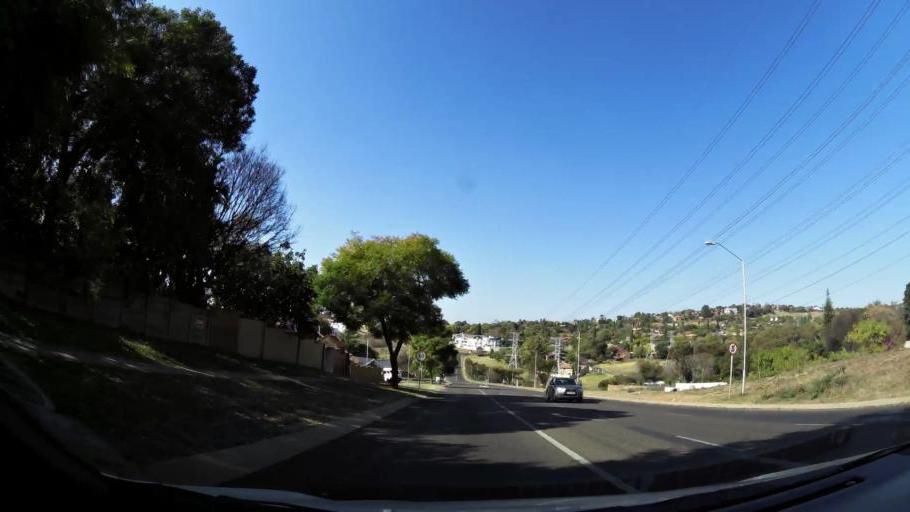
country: ZA
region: Gauteng
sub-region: City of Tshwane Metropolitan Municipality
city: Centurion
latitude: -25.8209
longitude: 28.2758
